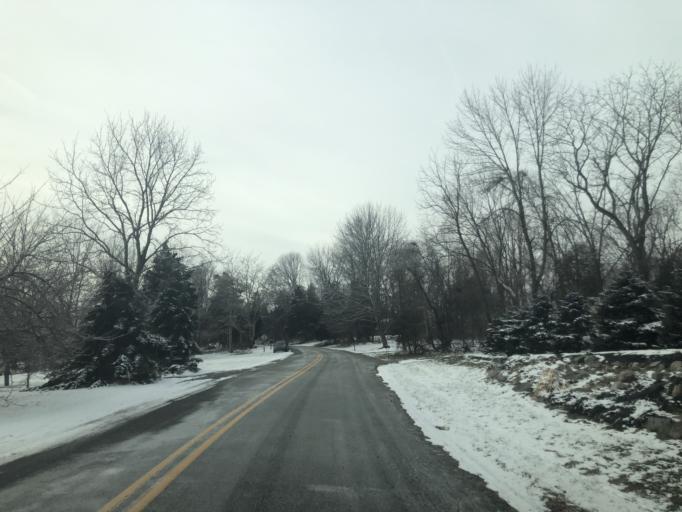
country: US
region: New Jersey
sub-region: Warren County
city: Belvidere
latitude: 40.9340
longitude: -75.0366
